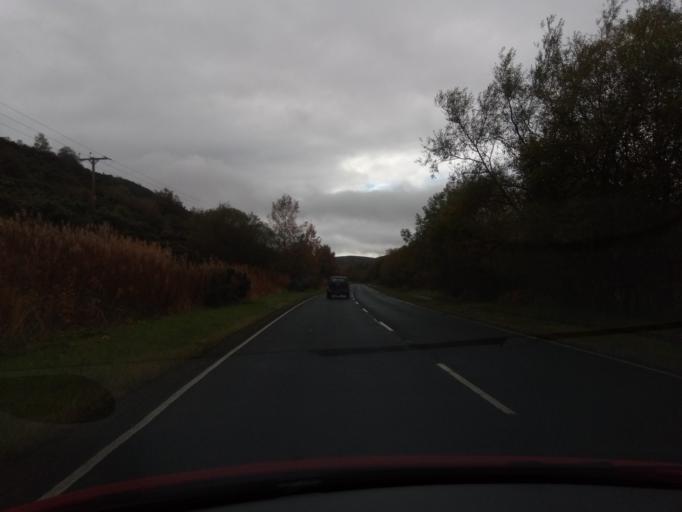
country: GB
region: Scotland
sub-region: The Scottish Borders
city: Galashiels
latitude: 55.6245
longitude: -2.8616
